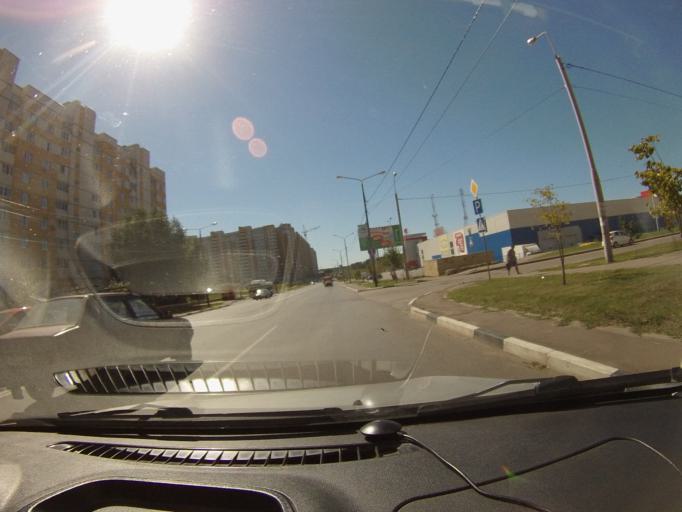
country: RU
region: Tambov
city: Tambov
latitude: 52.7667
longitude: 41.3997
